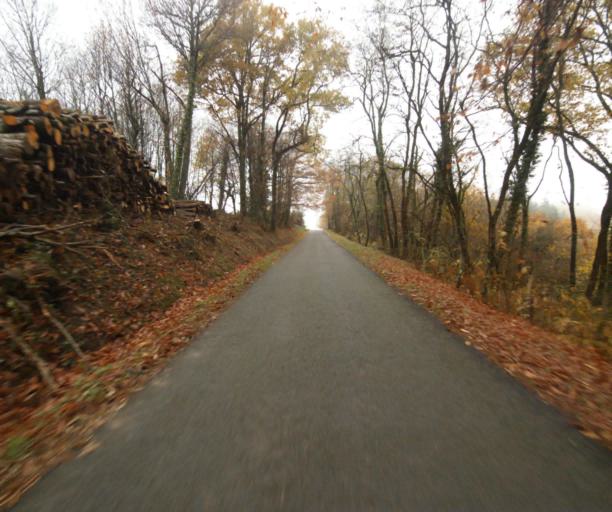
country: FR
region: Limousin
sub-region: Departement de la Correze
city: Cornil
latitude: 45.2001
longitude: 1.6404
